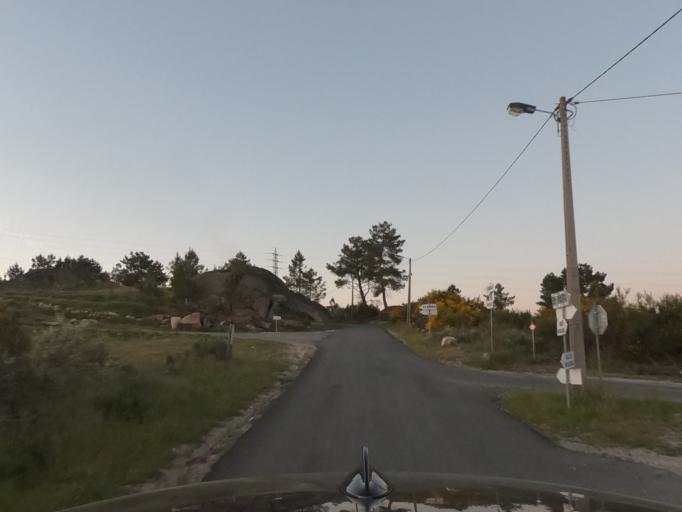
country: PT
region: Vila Real
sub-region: Vila Real
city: Vila Real
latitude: 41.3002
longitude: -7.6711
